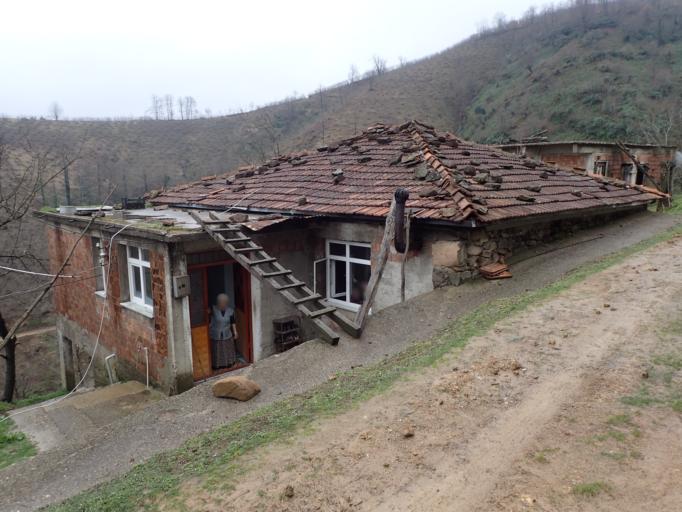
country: TR
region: Ordu
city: Camas
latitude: 40.8579
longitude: 37.5137
